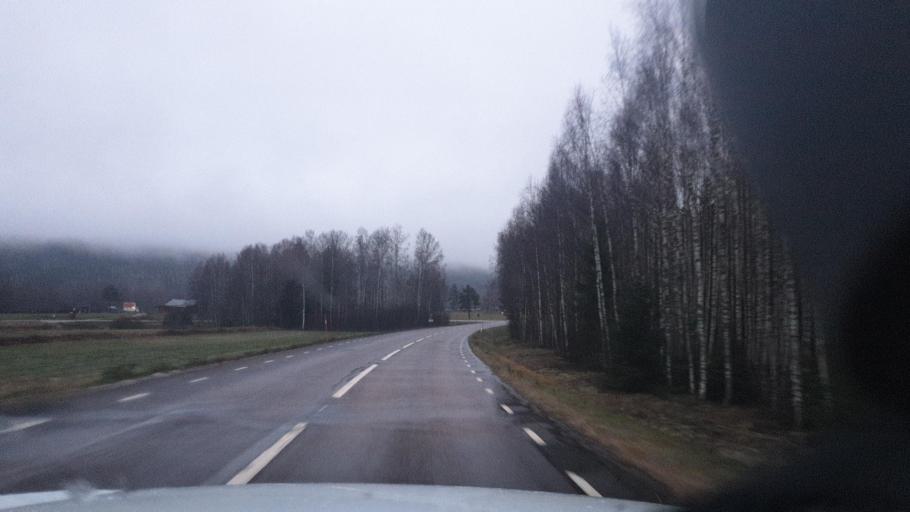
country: SE
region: Vaermland
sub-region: Eda Kommun
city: Amotfors
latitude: 59.6772
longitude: 12.3875
